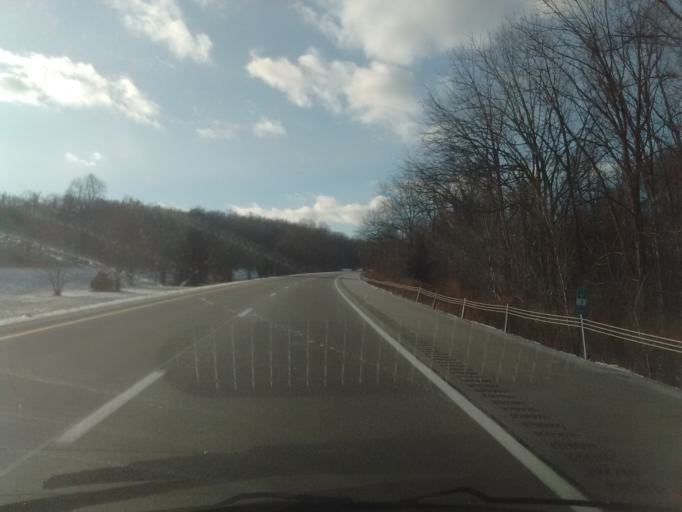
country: US
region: New York
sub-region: Dutchess County
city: Brinckerhoff
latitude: 41.5250
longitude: -73.8613
